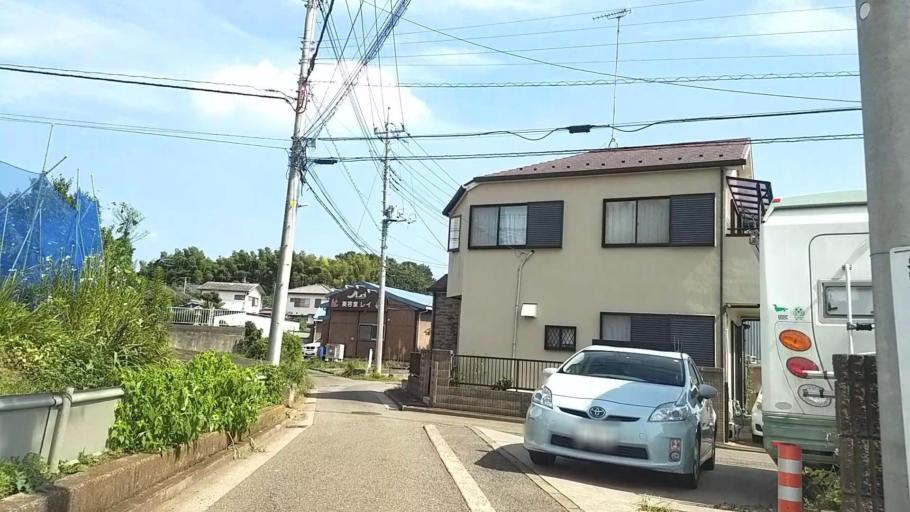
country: JP
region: Kanagawa
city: Yokohama
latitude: 35.5285
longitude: 139.6000
